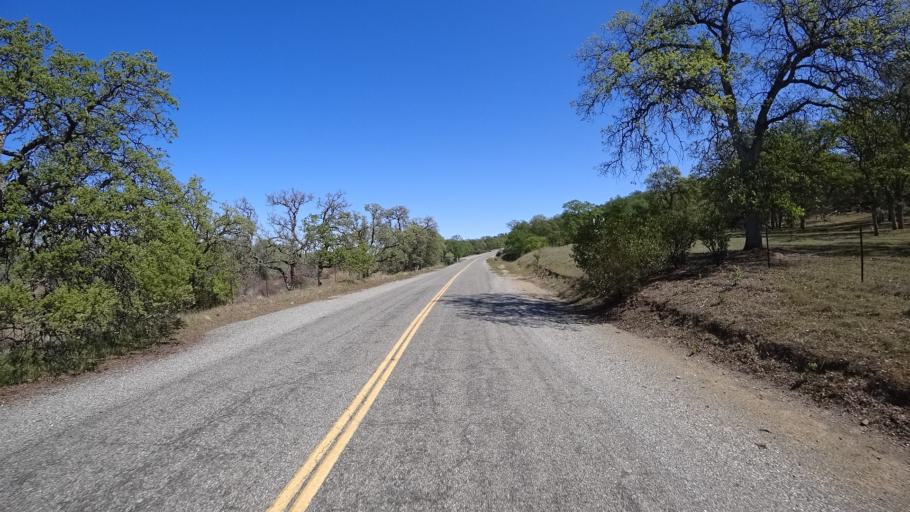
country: US
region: California
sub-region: Glenn County
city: Orland
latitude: 39.7389
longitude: -122.3905
